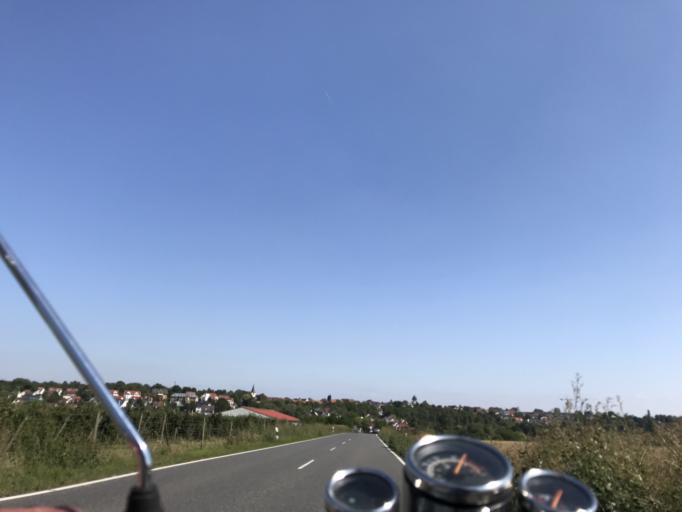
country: DE
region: Hesse
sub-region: Regierungsbezirk Darmstadt
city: Wiesbaden
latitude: 50.0817
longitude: 8.3151
